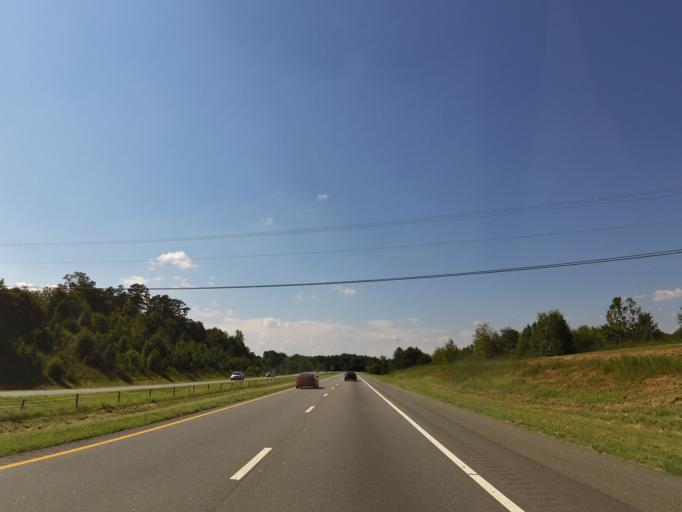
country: US
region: North Carolina
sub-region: Catawba County
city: Mountain View
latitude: 35.6869
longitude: -81.3460
